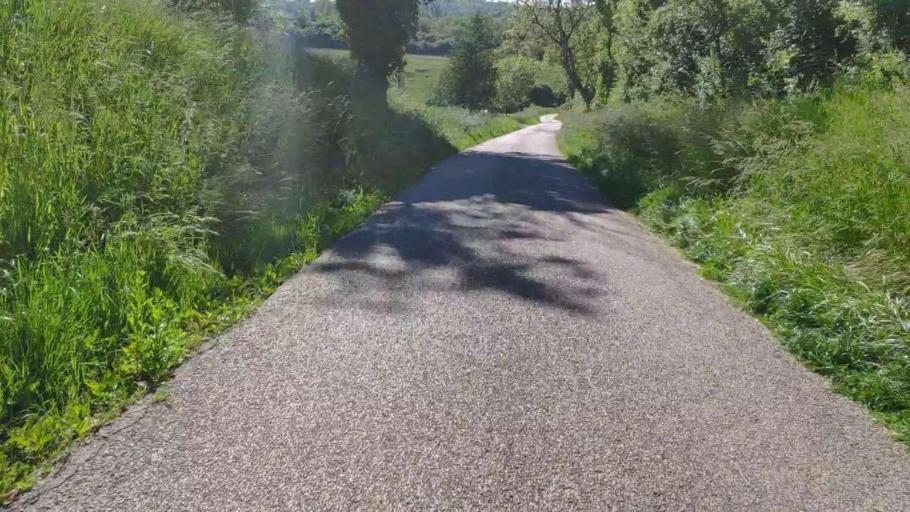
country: FR
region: Franche-Comte
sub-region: Departement du Jura
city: Lons-le-Saunier
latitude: 46.7273
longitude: 5.5620
